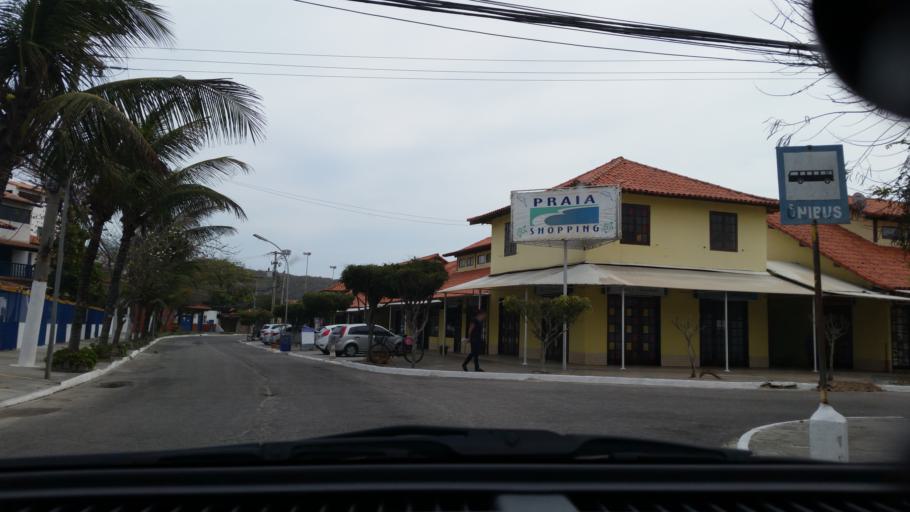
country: BR
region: Rio de Janeiro
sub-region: Cabo Frio
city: Cabo Frio
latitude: -22.8635
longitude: -41.9879
